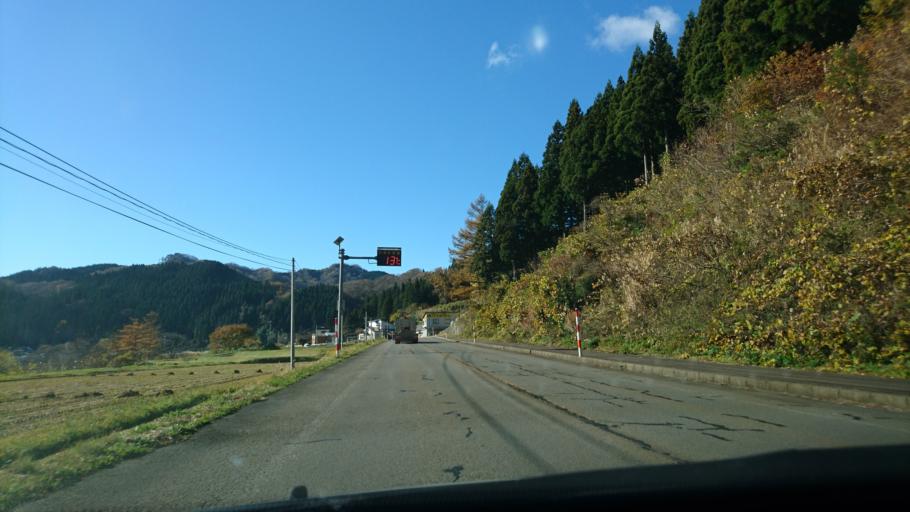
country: JP
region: Akita
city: Omagari
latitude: 39.3257
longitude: 140.1819
